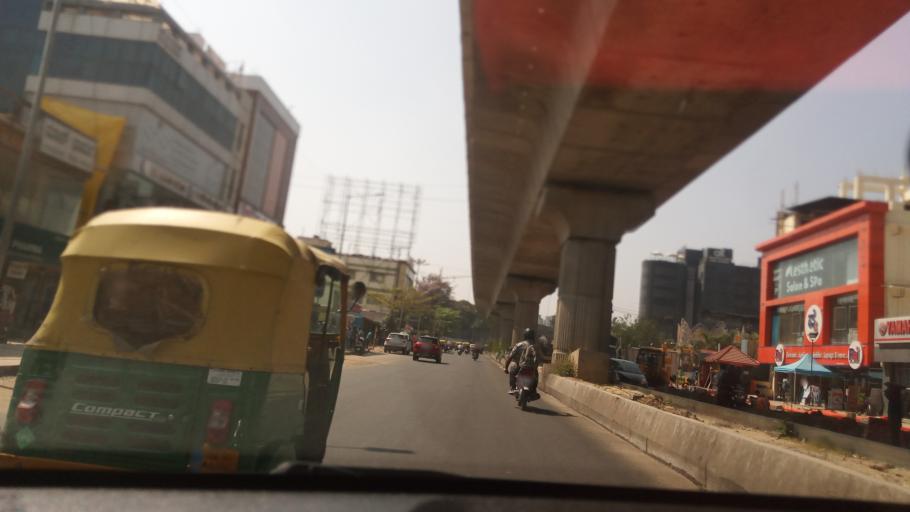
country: IN
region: Karnataka
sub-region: Bangalore Urban
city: Bangalore
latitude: 12.9951
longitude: 77.6974
